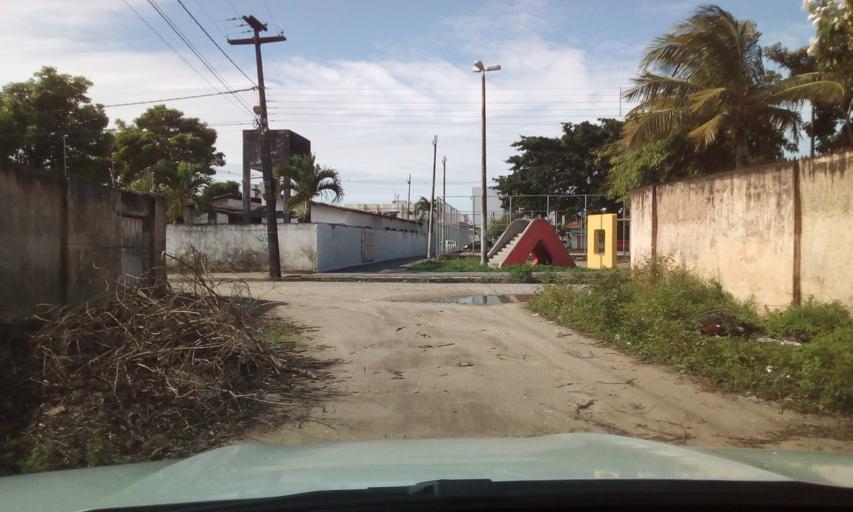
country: BR
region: Paraiba
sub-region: Joao Pessoa
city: Joao Pessoa
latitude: -7.1630
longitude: -34.8744
